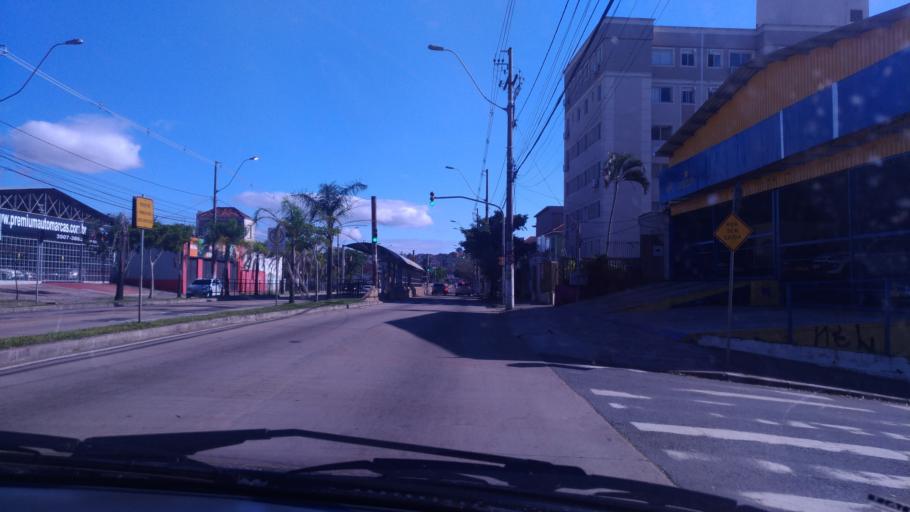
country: BR
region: Rio Grande do Sul
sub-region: Porto Alegre
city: Porto Alegre
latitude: -30.0731
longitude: -51.1986
